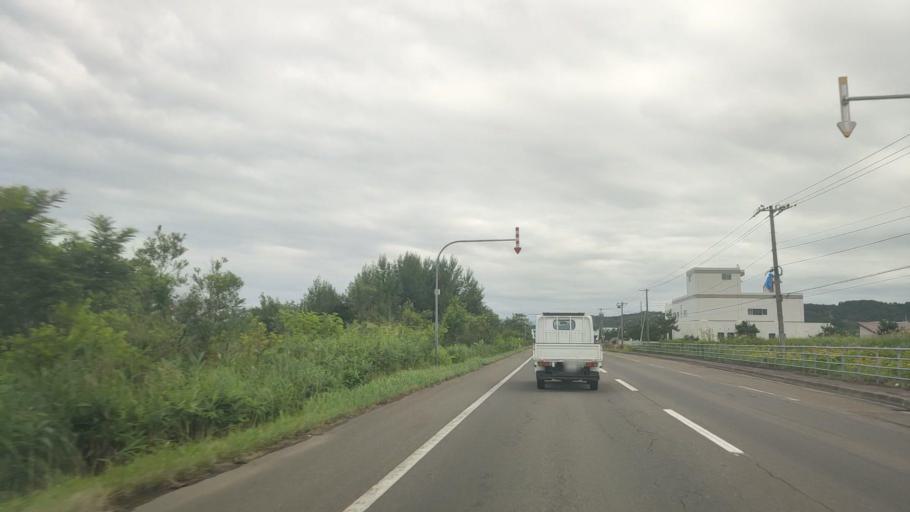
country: JP
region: Hokkaido
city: Niseko Town
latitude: 42.3887
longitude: 140.2973
